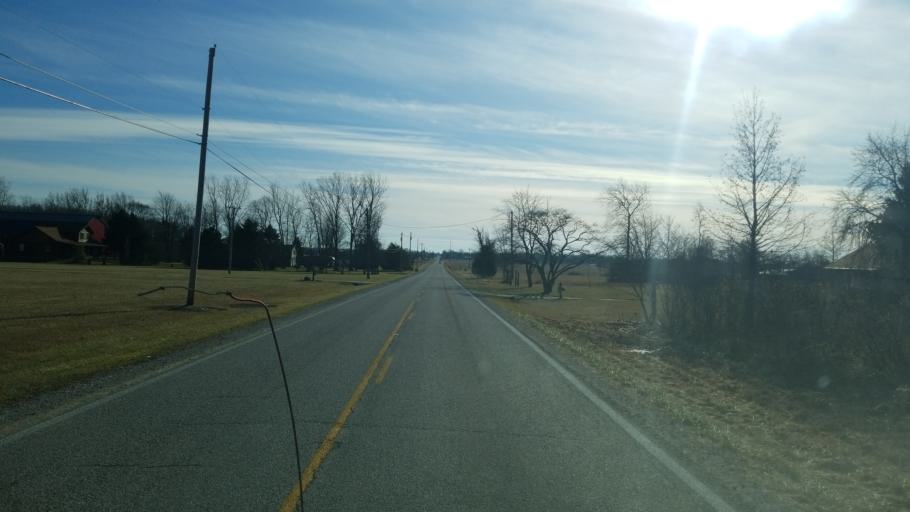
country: US
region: Ohio
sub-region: Sandusky County
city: Stony Prairie
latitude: 41.3764
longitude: -83.2226
